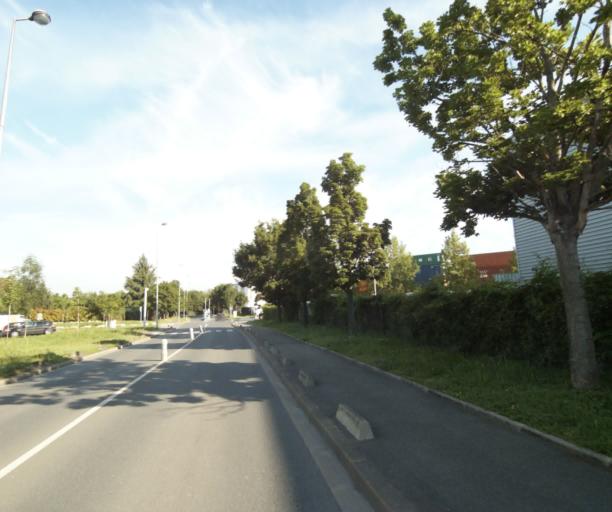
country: FR
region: Ile-de-France
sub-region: Departement du Val-d'Oise
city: Argenteuil
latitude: 48.9371
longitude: 2.2652
